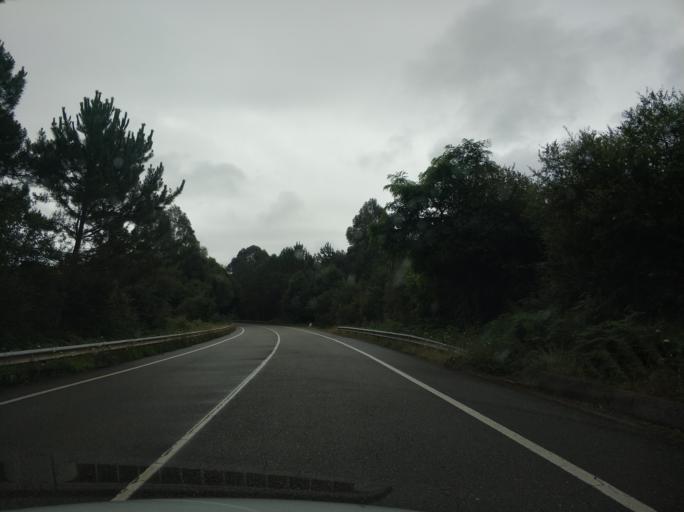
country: ES
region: Asturias
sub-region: Province of Asturias
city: Tineo
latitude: 43.5410
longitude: -6.4250
